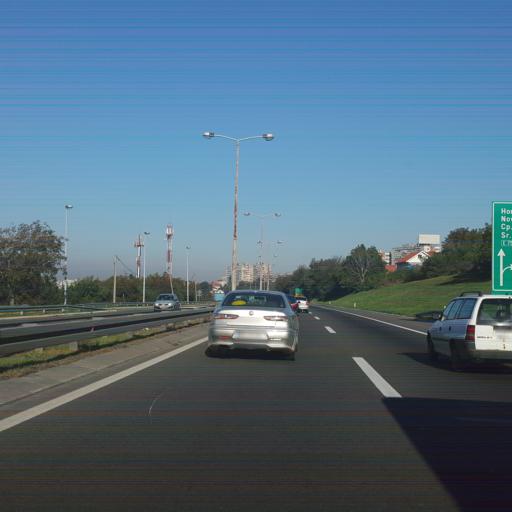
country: RS
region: Central Serbia
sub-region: Belgrade
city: Zvezdara
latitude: 44.7765
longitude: 20.5138
